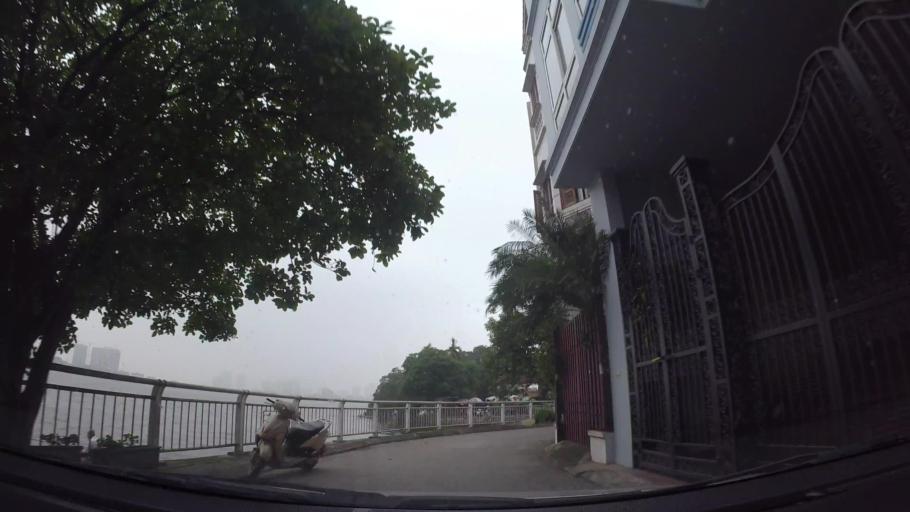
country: VN
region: Ha Noi
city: Tay Ho
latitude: 21.0546
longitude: 105.8201
